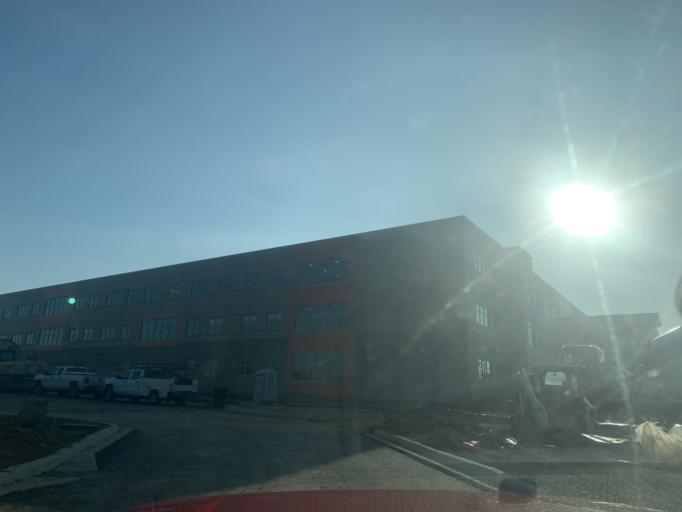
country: US
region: Maryland
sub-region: Anne Arundel County
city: Brooklyn Park
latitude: 39.2267
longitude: -76.5995
